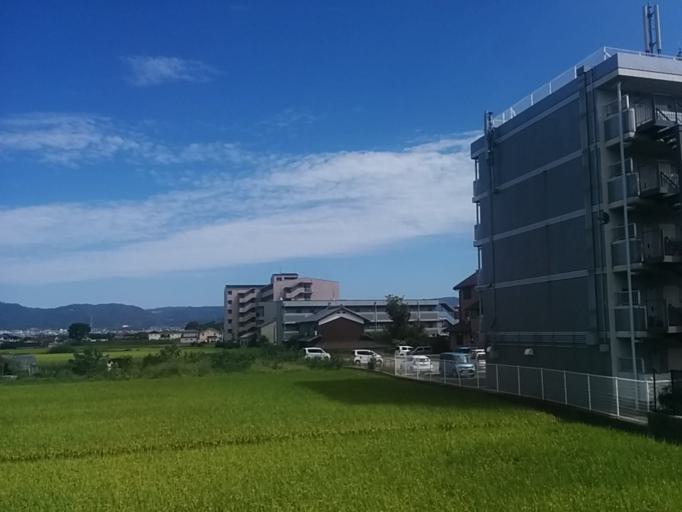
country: JP
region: Nara
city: Nara-shi
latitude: 34.6606
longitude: 135.7833
